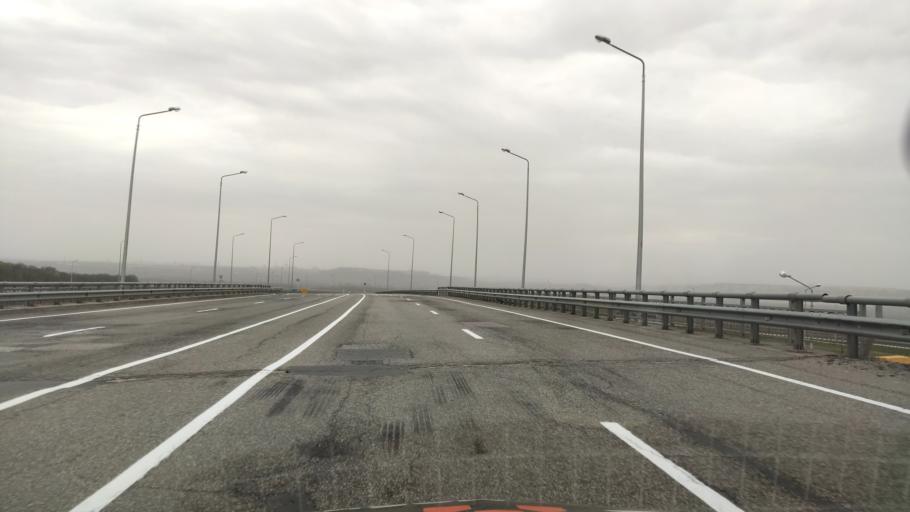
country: RU
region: Belgorod
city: Staryy Oskol
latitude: 51.3270
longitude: 37.7403
